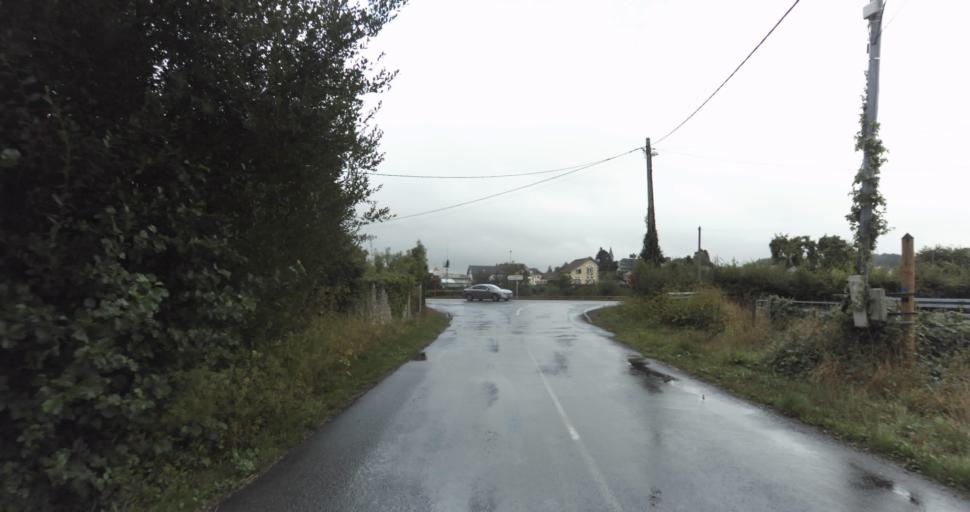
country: FR
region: Lower Normandy
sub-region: Departement de l'Orne
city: Sainte-Gauburge-Sainte-Colombe
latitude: 48.7185
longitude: 0.4306
